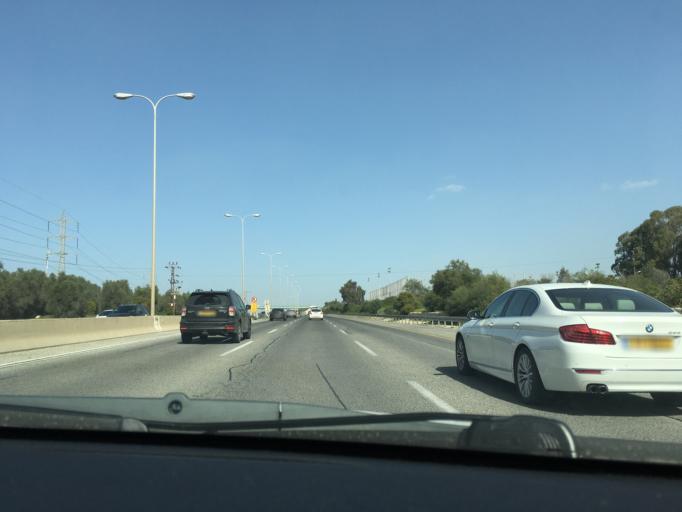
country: IL
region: Central District
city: Hod HaSharon
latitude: 32.1363
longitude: 34.8714
